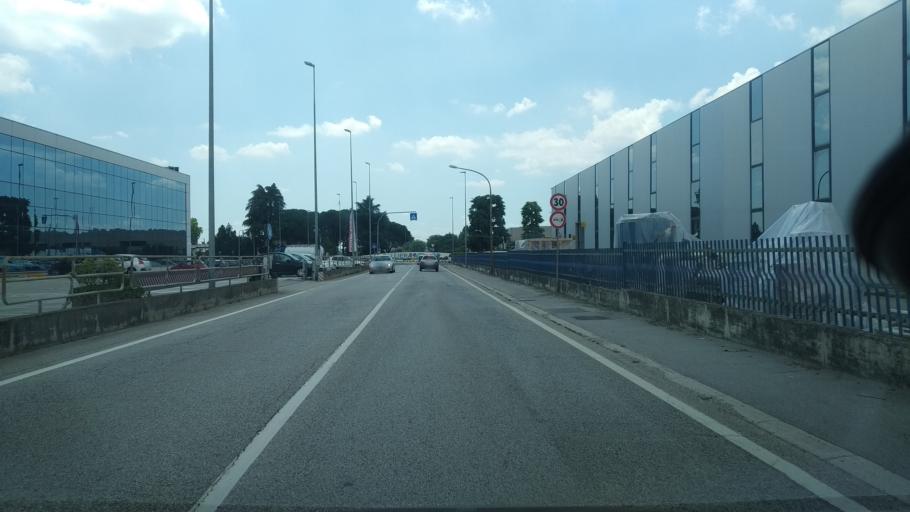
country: IT
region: Veneto
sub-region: Provincia di Padova
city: Galliera Veneta
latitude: 45.6666
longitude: 11.8183
